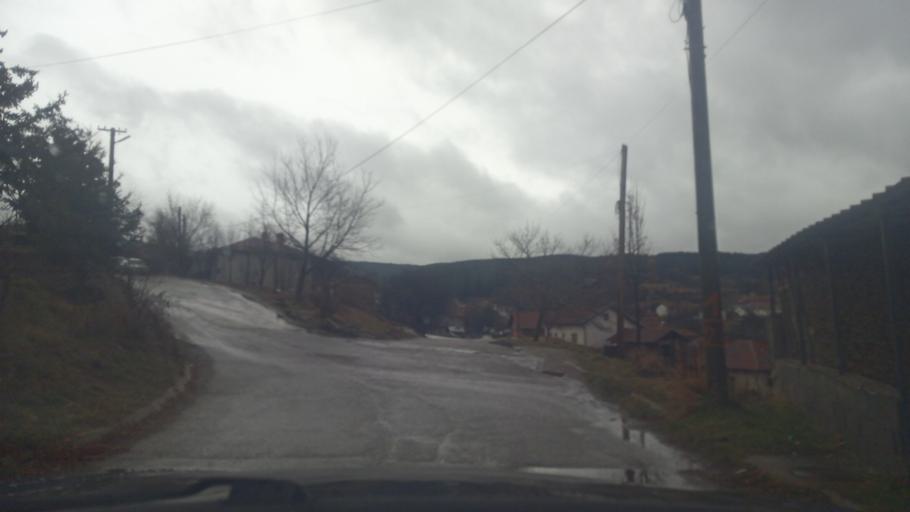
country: MK
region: Pehcevo
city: Pehcevo
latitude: 41.7638
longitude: 22.8909
